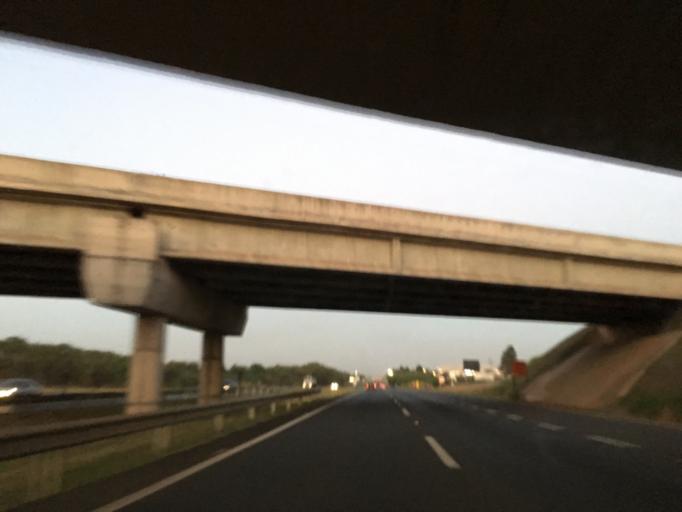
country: BR
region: Sao Paulo
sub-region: Piracicaba
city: Piracicaba
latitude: -22.7217
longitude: -47.6068
